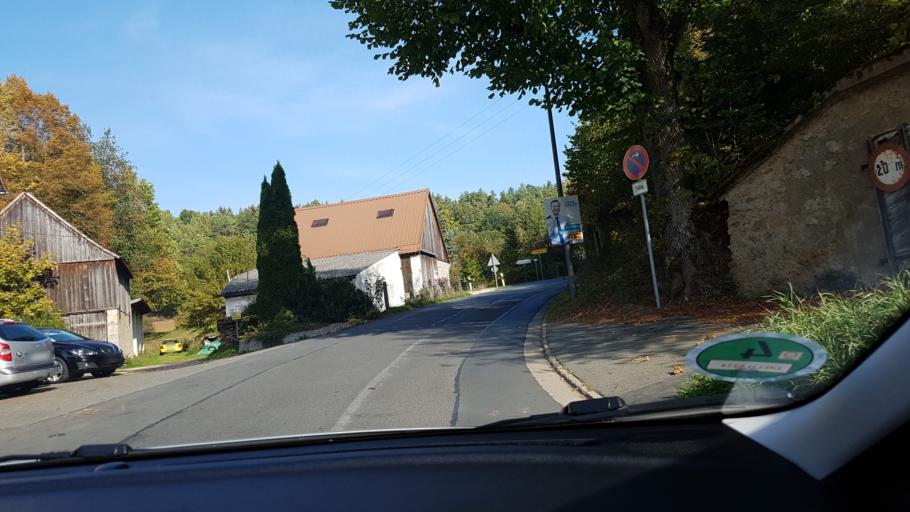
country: DE
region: Bavaria
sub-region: Upper Franconia
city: Waischenfeld
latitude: 49.8141
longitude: 11.3534
